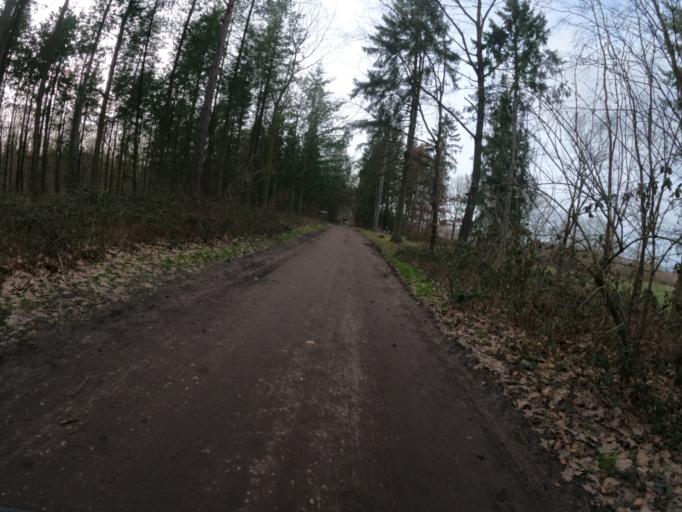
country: DE
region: Schleswig-Holstein
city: Appen
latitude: 53.6126
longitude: 9.7545
